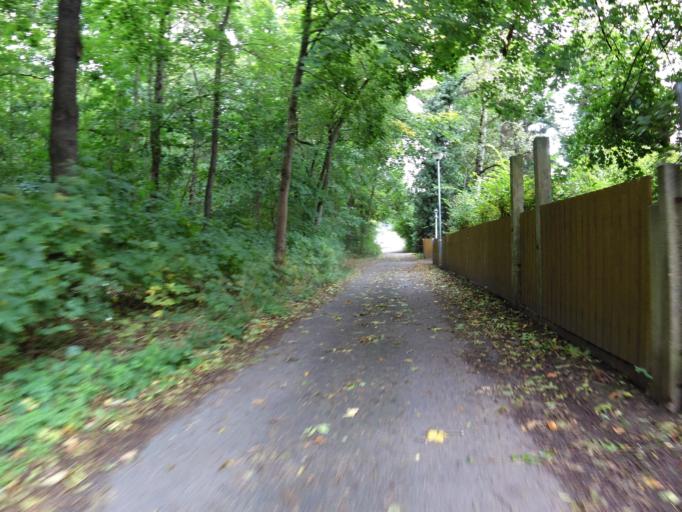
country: DE
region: Saxony
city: Markkleeberg
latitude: 51.2903
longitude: 12.3675
